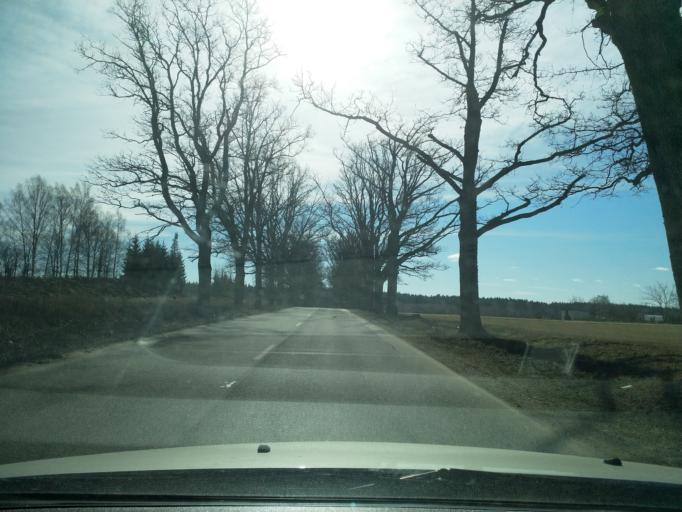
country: LV
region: Valmieras Rajons
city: Valmiera
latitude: 57.5162
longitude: 25.4209
